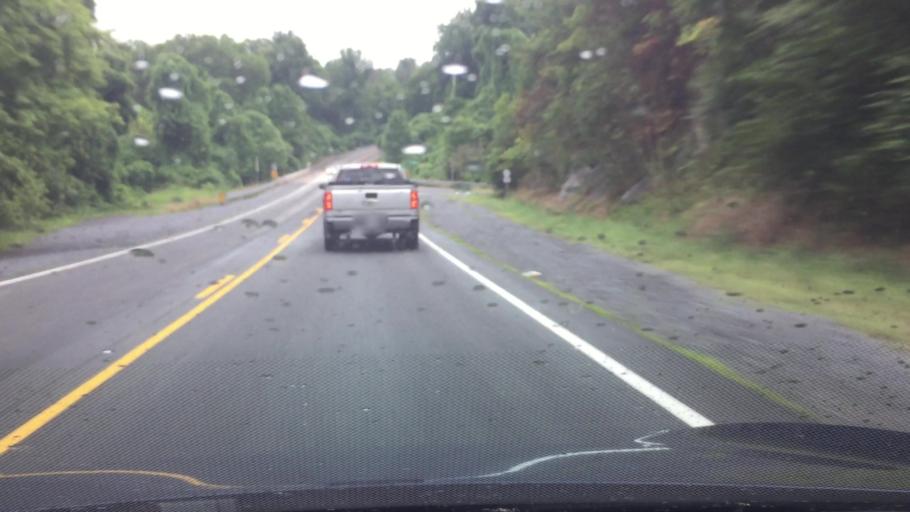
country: US
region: Virginia
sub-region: City of Bedford
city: Bedford
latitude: 37.3652
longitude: -79.4180
